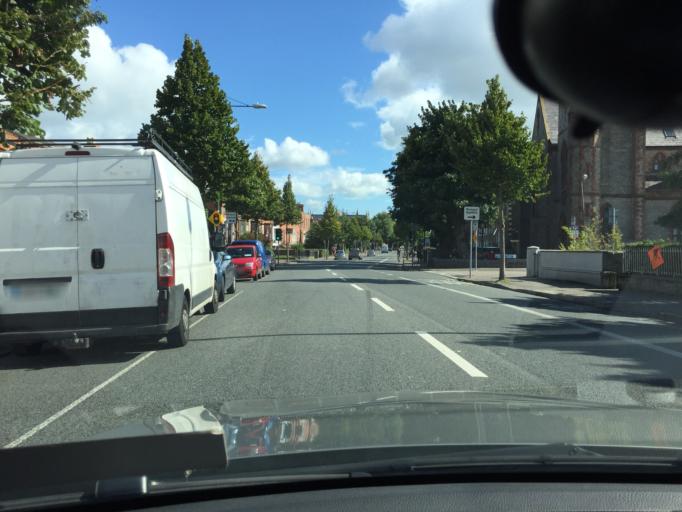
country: IE
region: Leinster
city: Rathmines
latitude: 53.3322
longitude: -6.2726
